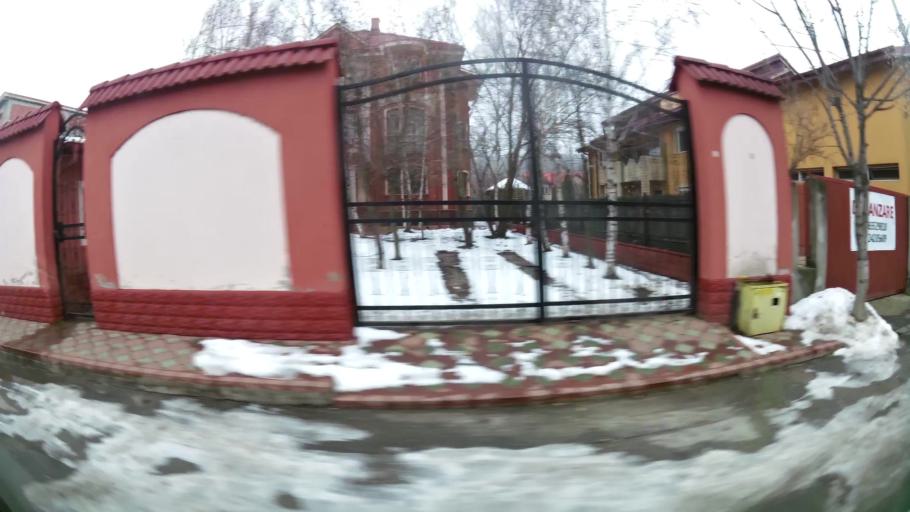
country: RO
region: Ilfov
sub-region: Comuna Chiajna
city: Rosu
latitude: 44.4531
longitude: 26.0038
